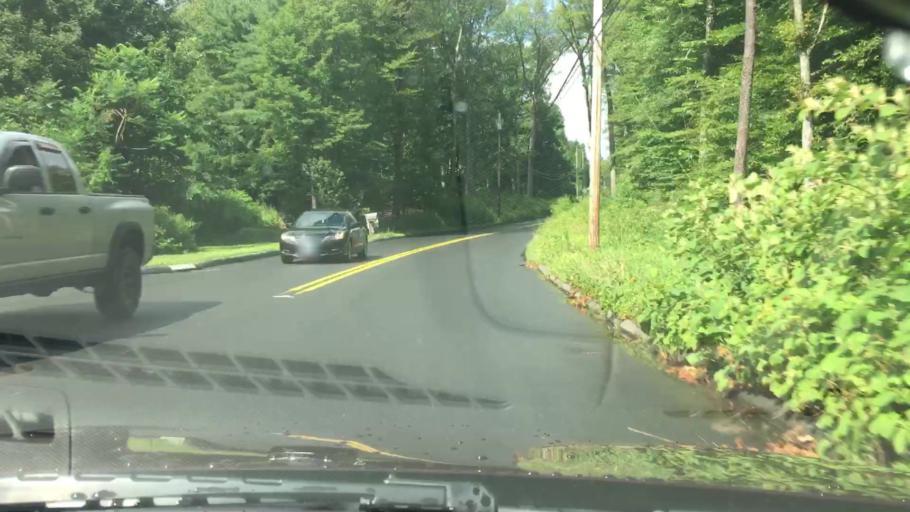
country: US
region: Connecticut
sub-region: Hartford County
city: Manchester
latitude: 41.7254
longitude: -72.5368
